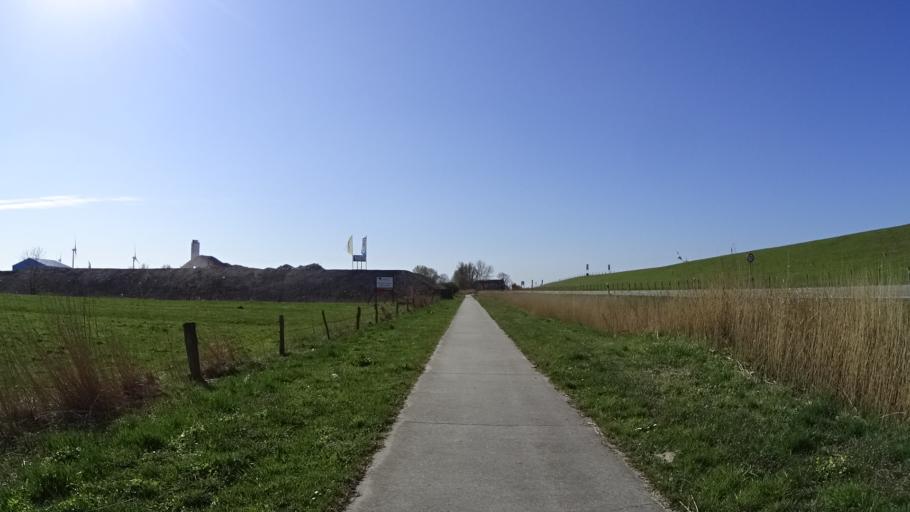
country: DE
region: Lower Saxony
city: Jemgum
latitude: 53.2667
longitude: 7.4076
